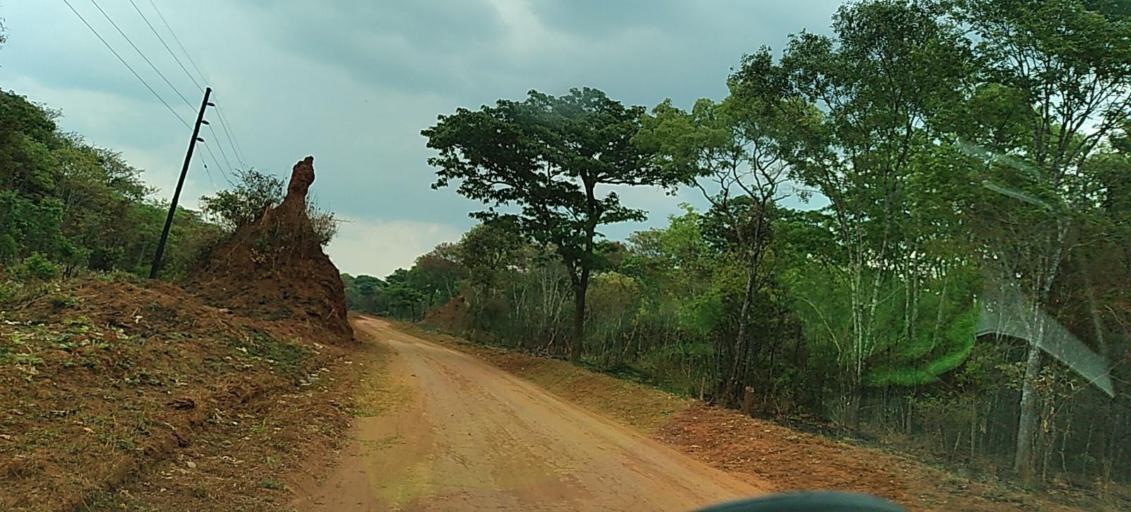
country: ZM
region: North-Western
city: Solwezi
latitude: -12.7811
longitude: 26.4901
